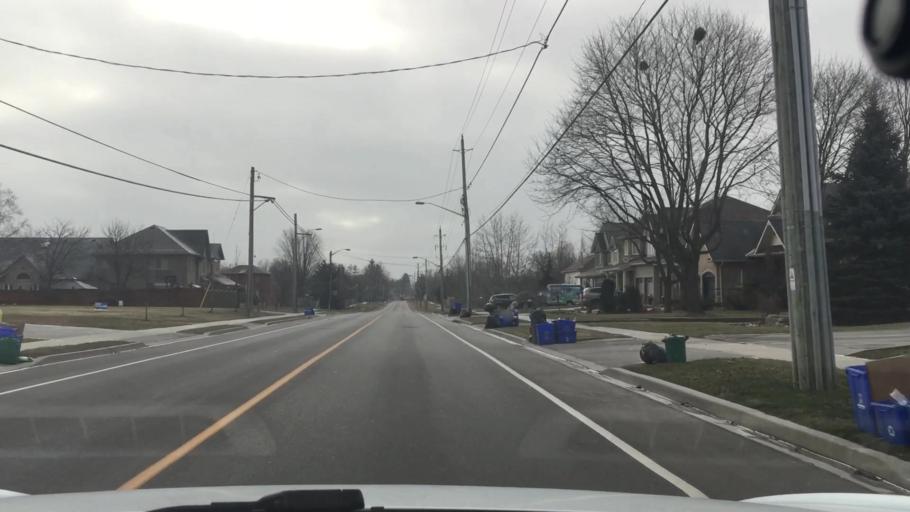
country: CA
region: Ontario
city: Oshawa
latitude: 43.9204
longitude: -78.7926
